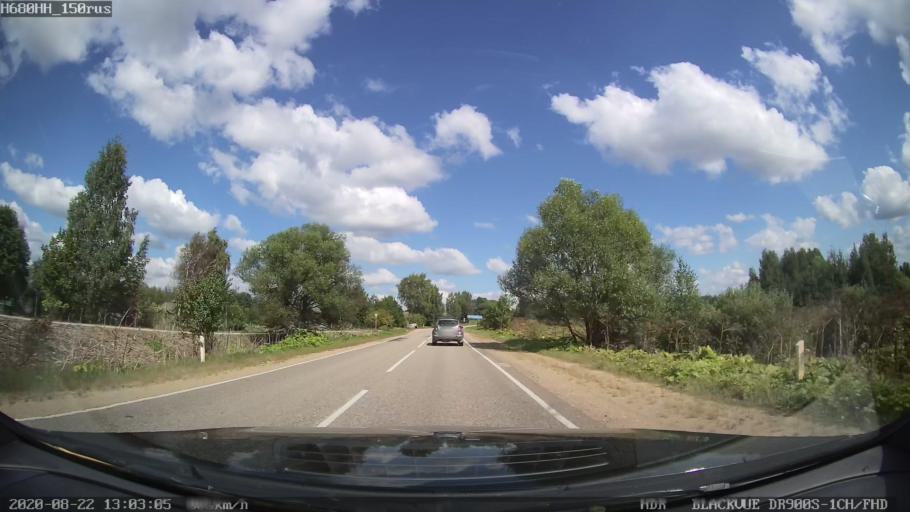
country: RU
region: Tverskaya
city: Bezhetsk
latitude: 57.6571
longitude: 36.4064
